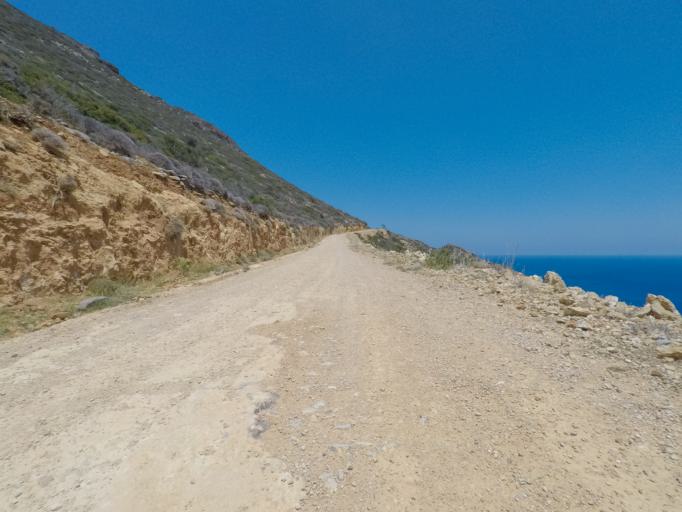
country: GR
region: Crete
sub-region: Nomos Lasithiou
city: Elounda
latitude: 35.3160
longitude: 25.7518
